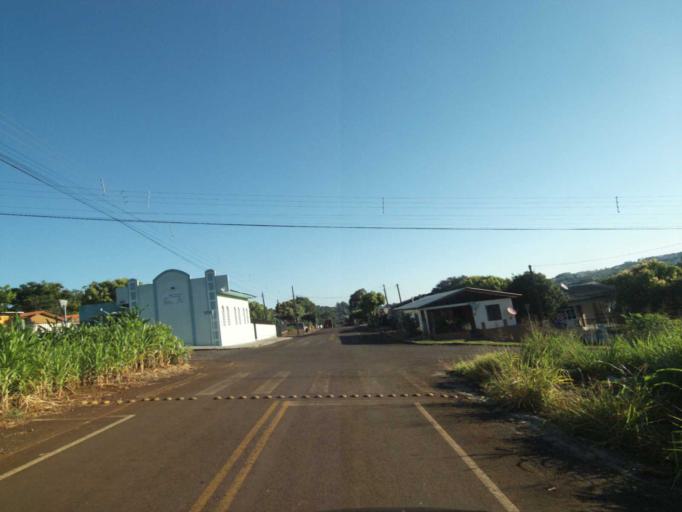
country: BR
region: Parana
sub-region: Coronel Vivida
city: Coronel Vivida
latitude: -25.9603
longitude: -52.8131
